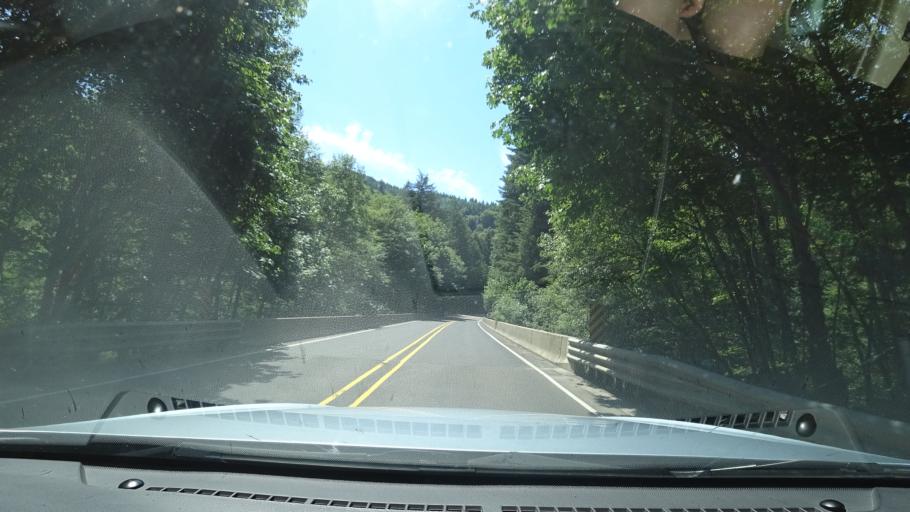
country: US
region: Oregon
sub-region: Lane County
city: Veneta
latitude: 43.9990
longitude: -123.6363
